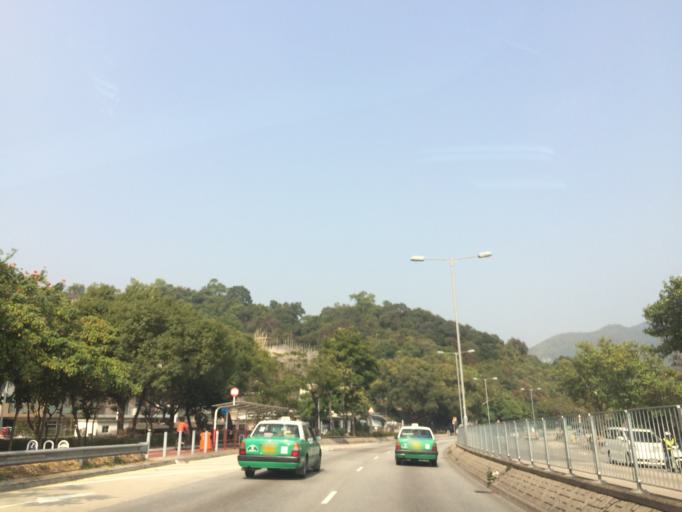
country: HK
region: Tai Po
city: Tai Po
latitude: 22.4573
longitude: 114.1775
